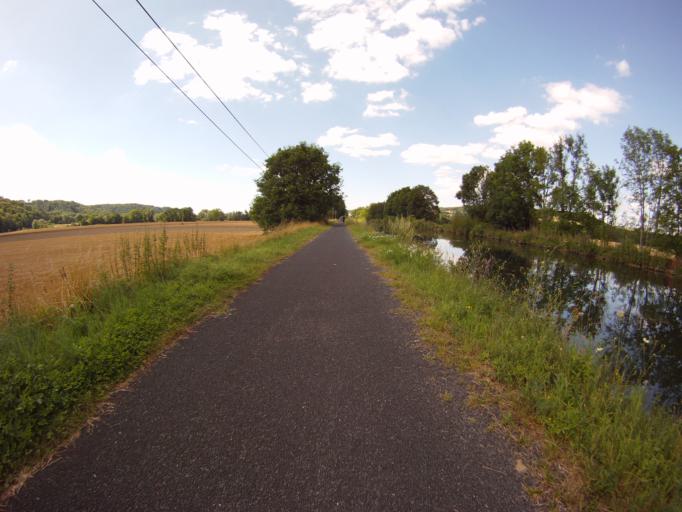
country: FR
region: Lorraine
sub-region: Departement de la Meuse
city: Longeville-en-Barrois
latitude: 48.7467
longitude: 5.1959
